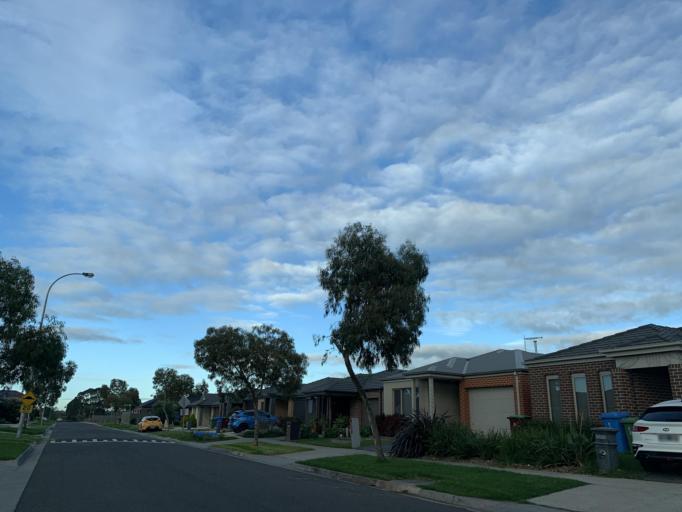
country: AU
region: Victoria
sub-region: Casey
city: Cranbourne East
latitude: -38.1256
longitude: 145.3046
